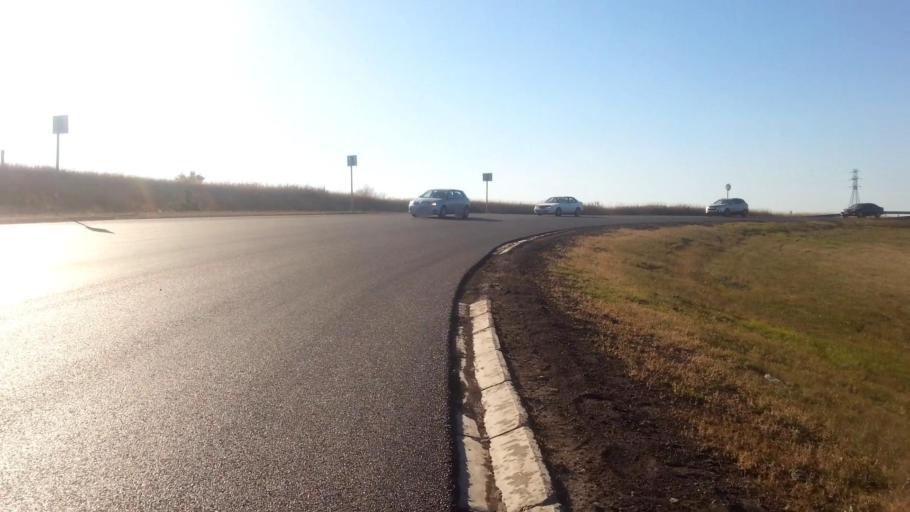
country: RU
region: Altai Krai
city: Novoaltaysk
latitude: 53.3700
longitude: 83.9565
